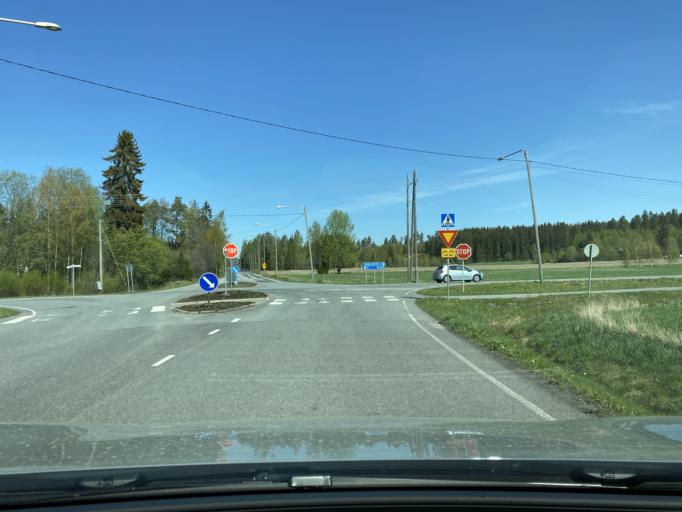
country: FI
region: Pirkanmaa
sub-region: Lounais-Pirkanmaa
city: Vammala
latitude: 61.3524
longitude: 22.8698
